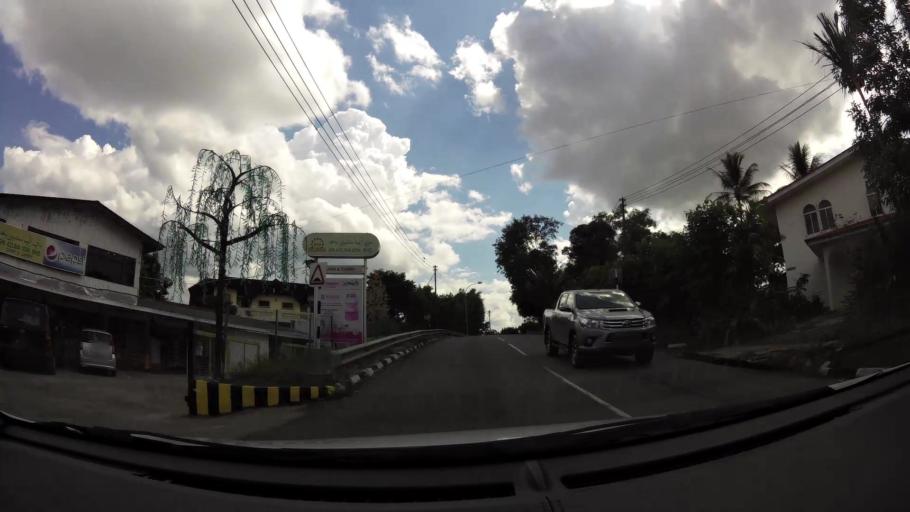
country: BN
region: Brunei and Muara
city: Bandar Seri Begawan
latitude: 4.9574
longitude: 114.9613
